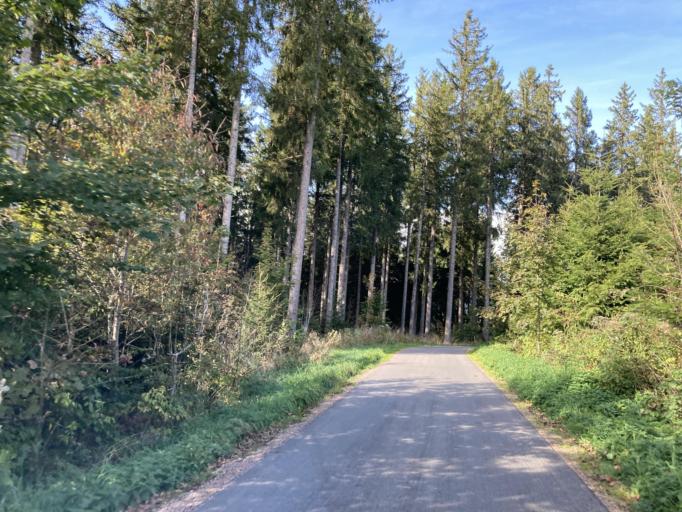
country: DE
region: Baden-Wuerttemberg
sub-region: Freiburg Region
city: Vohrenbach
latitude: 48.0828
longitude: 8.2783
